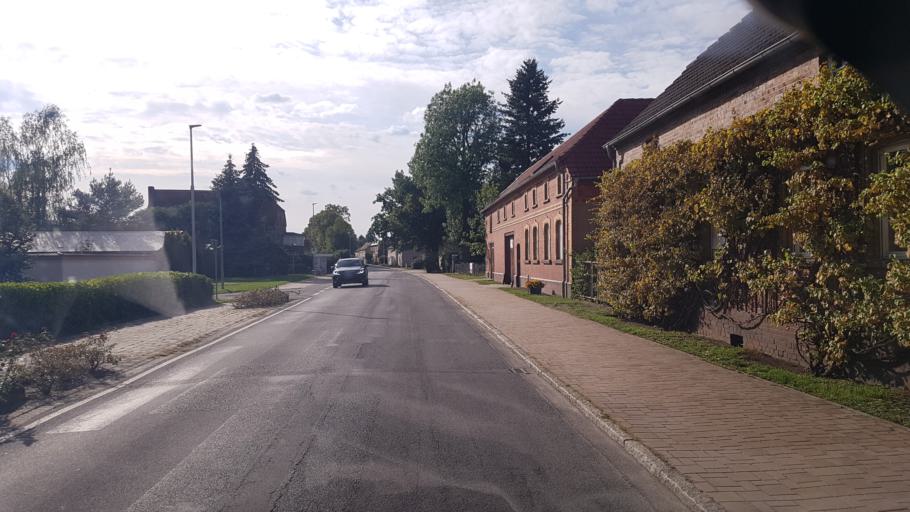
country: DE
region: Brandenburg
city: Welzow
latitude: 51.5518
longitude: 14.1912
